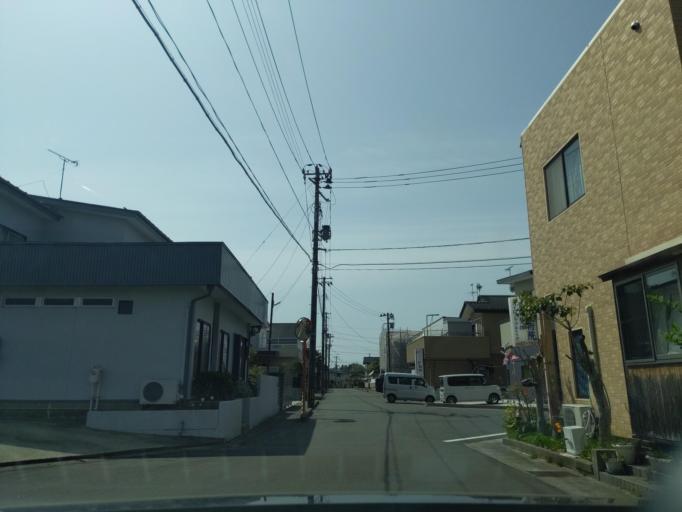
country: JP
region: Fukushima
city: Koriyama
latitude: 37.3723
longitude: 140.3605
